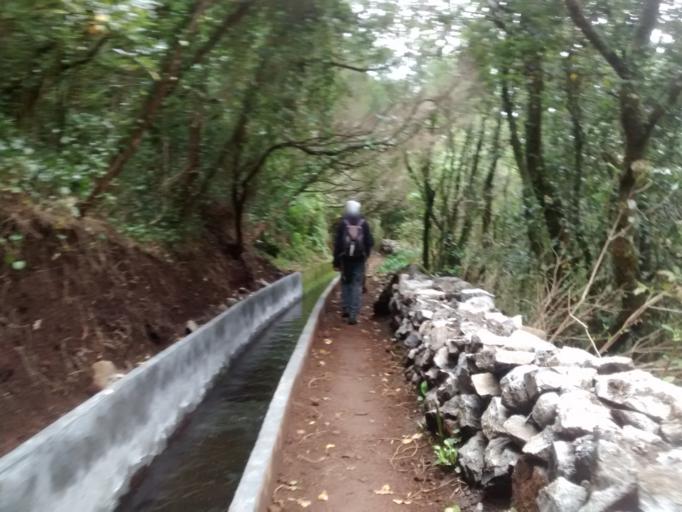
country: PT
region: Madeira
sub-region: Sao Vicente
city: Sao Vicente
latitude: 32.7582
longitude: -17.0479
